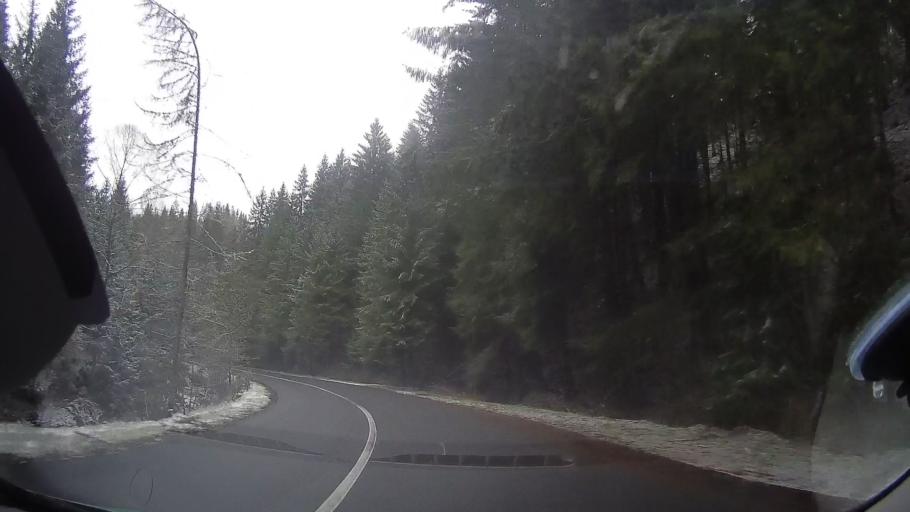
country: RO
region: Cluj
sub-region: Comuna Calatele
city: Calatele
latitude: 46.7318
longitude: 23.0394
